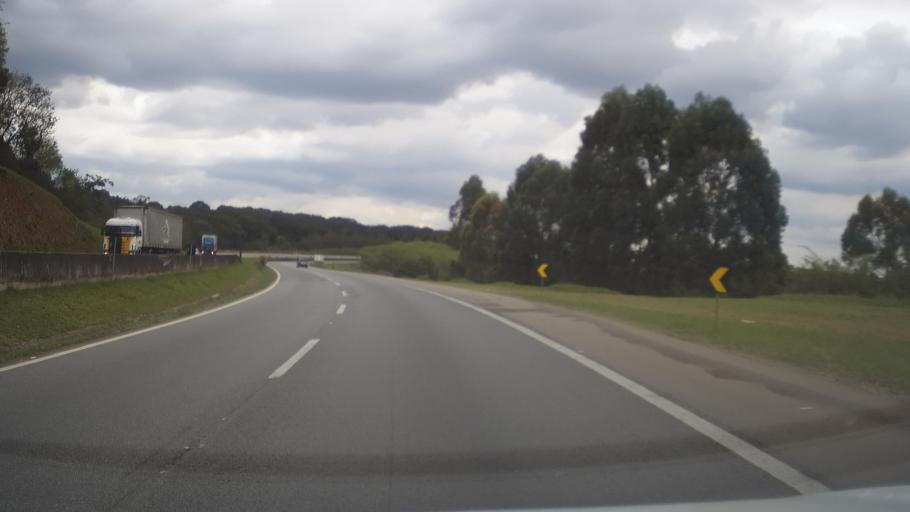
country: BR
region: Minas Gerais
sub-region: Tres Coracoes
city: Tres Coracoes
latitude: -21.4943
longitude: -45.2103
